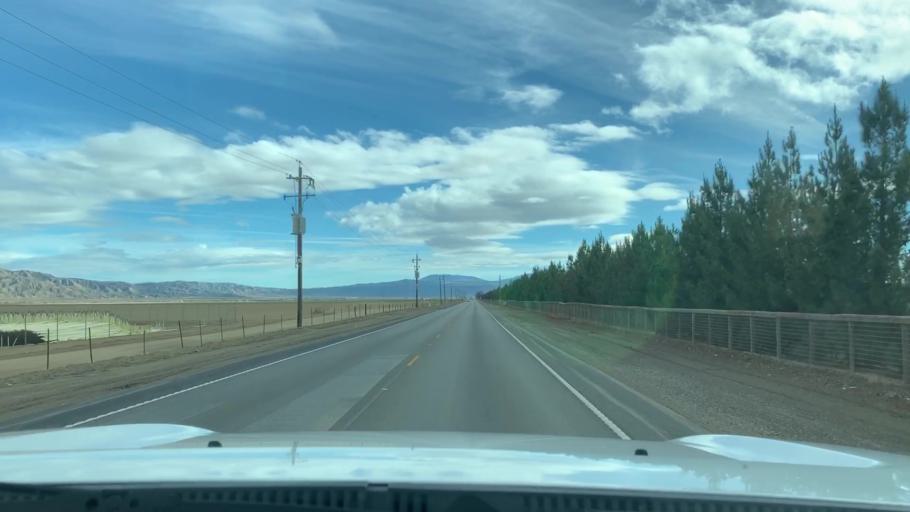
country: US
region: California
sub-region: Kern County
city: Taft Heights
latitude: 34.9434
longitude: -119.6649
